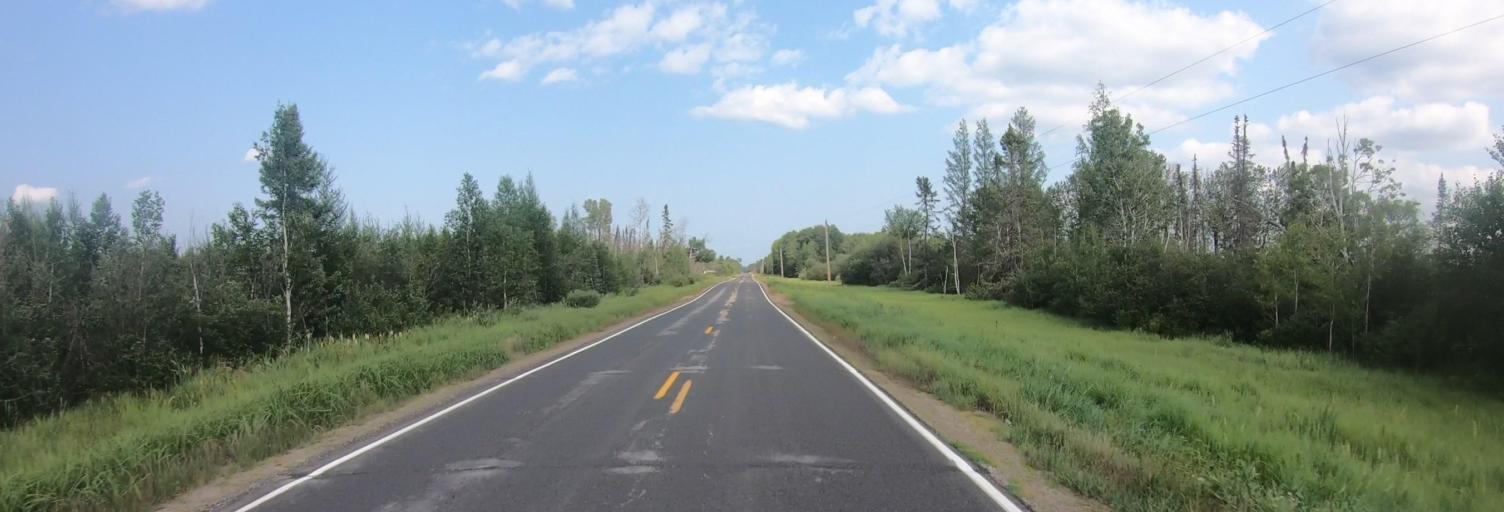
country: US
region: Minnesota
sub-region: Saint Louis County
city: Mountain Iron
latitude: 47.8916
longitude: -92.6784
